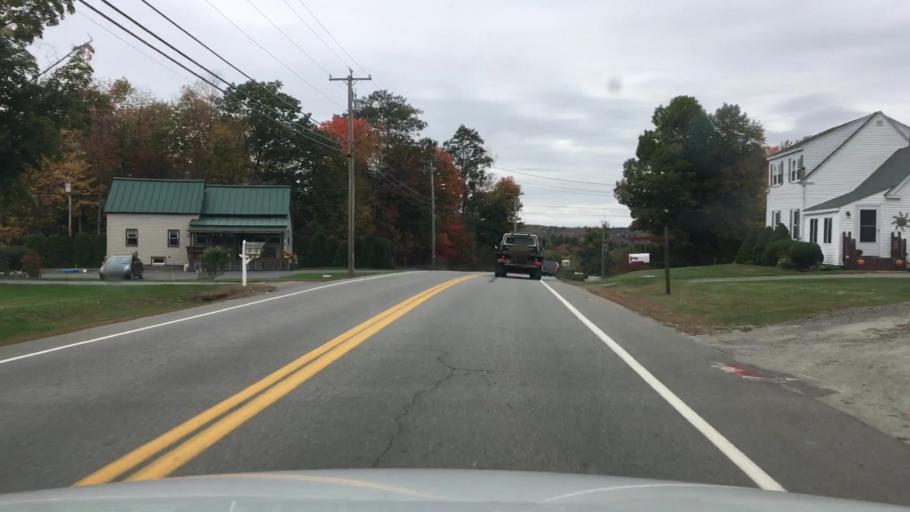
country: US
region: Maine
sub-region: Kennebec County
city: Oakland
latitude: 44.5563
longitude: -69.7407
